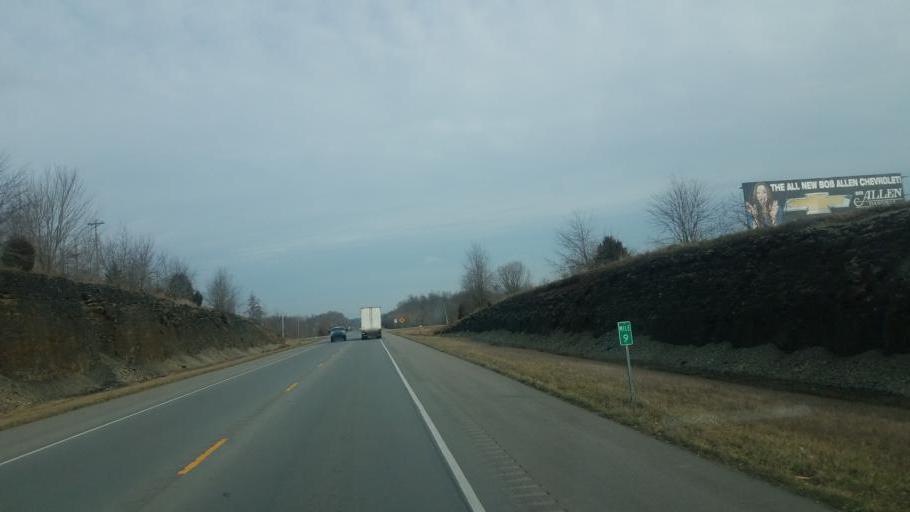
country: US
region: Kentucky
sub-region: Boyle County
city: Junction City
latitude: 37.5467
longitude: -84.8017
